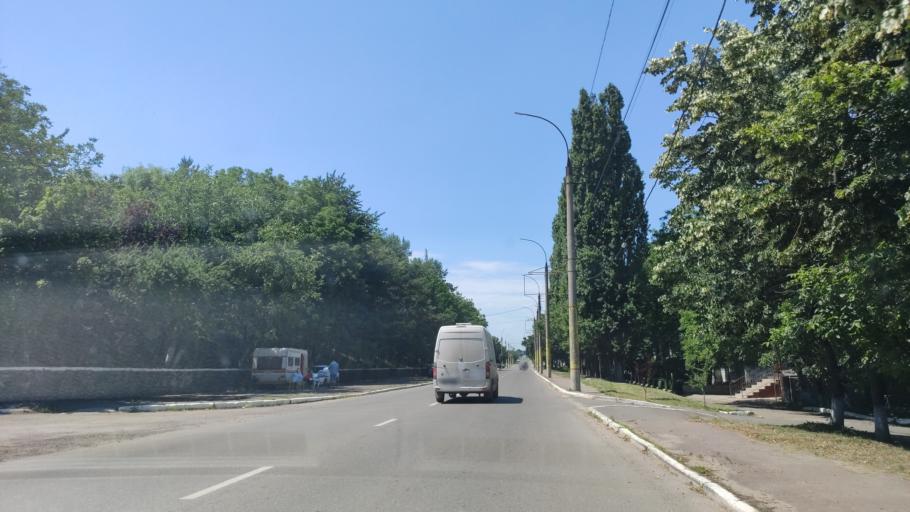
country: MD
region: Raionul Soroca
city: Soroca
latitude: 48.1625
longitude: 28.2723
